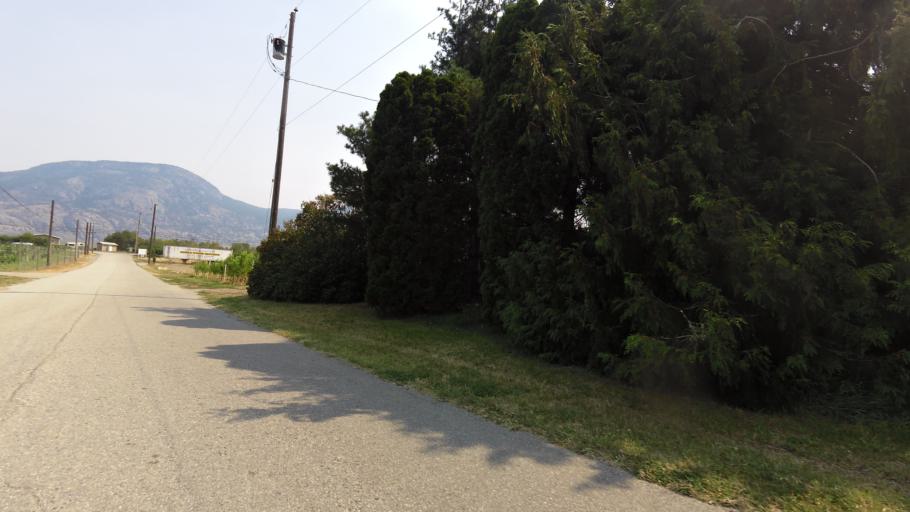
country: CA
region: British Columbia
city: Osoyoos
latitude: 49.0531
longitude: -119.5064
